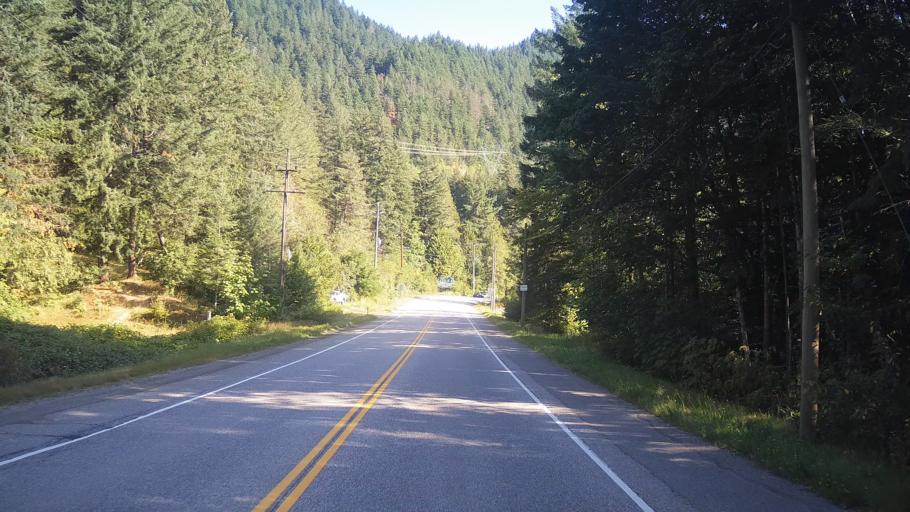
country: CA
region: British Columbia
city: Hope
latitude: 49.5547
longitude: -121.4449
